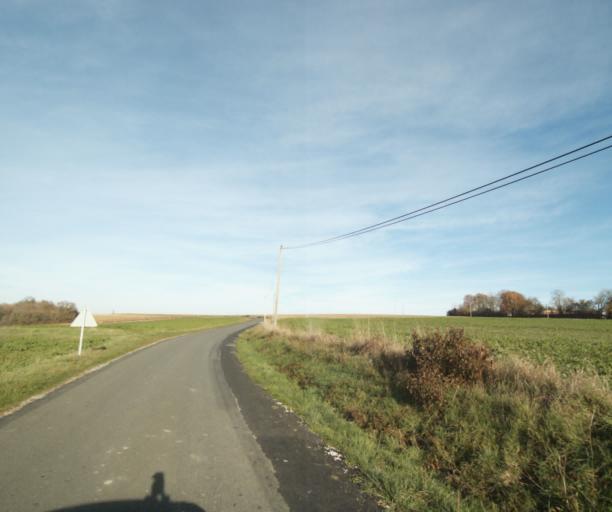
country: FR
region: Poitou-Charentes
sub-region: Departement de la Charente-Maritime
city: Chaniers
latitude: 45.7149
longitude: -0.5304
